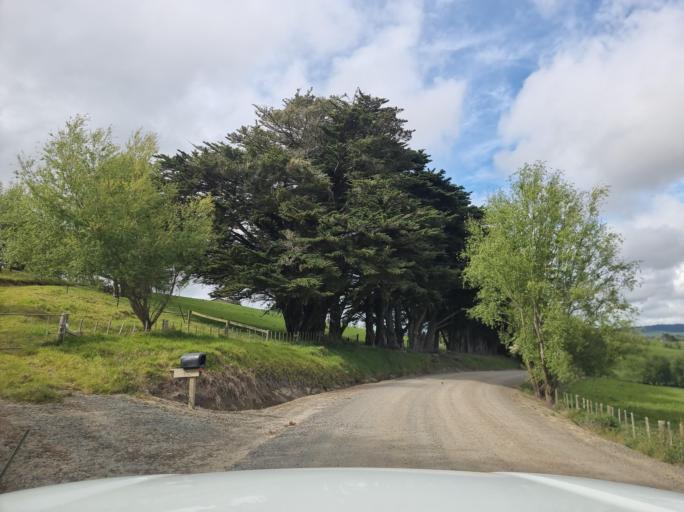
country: NZ
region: Northland
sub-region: Whangarei
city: Ruakaka
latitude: -36.1179
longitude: 174.2107
